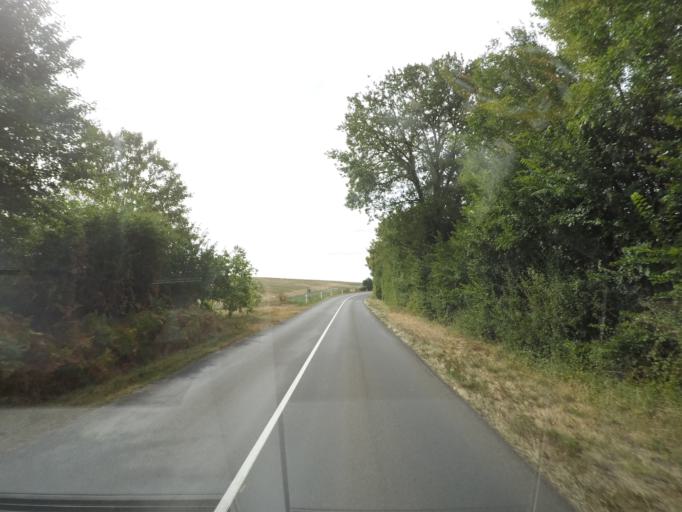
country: FR
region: Poitou-Charentes
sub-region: Departement de la Charente
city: Nanteuil-en-Vallee
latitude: 45.9863
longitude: 0.3457
